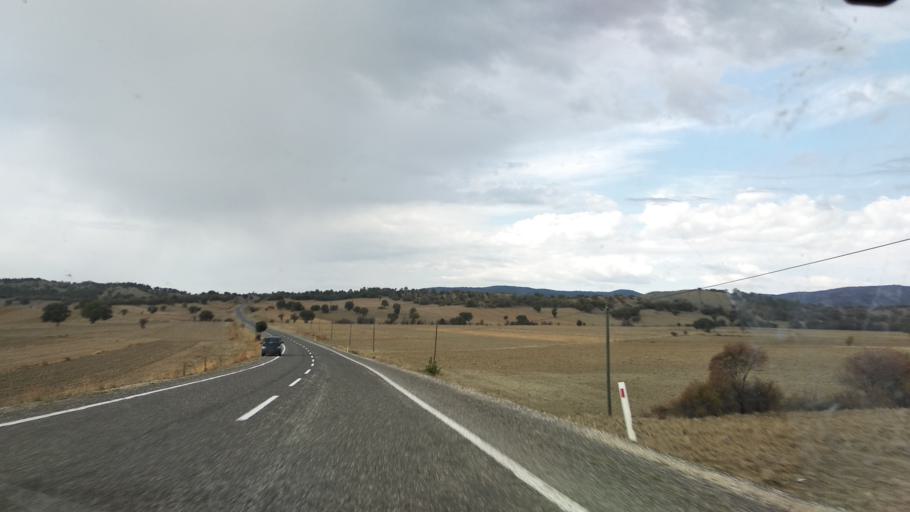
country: TR
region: Bolu
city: Seben
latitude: 40.3329
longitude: 31.4553
